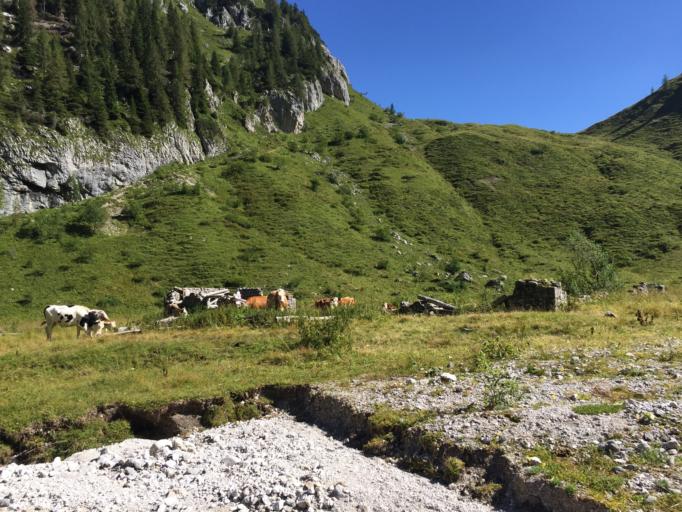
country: IT
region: Friuli Venezia Giulia
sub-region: Provincia di Udine
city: Forni Avoltri
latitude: 46.5494
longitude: 12.7423
